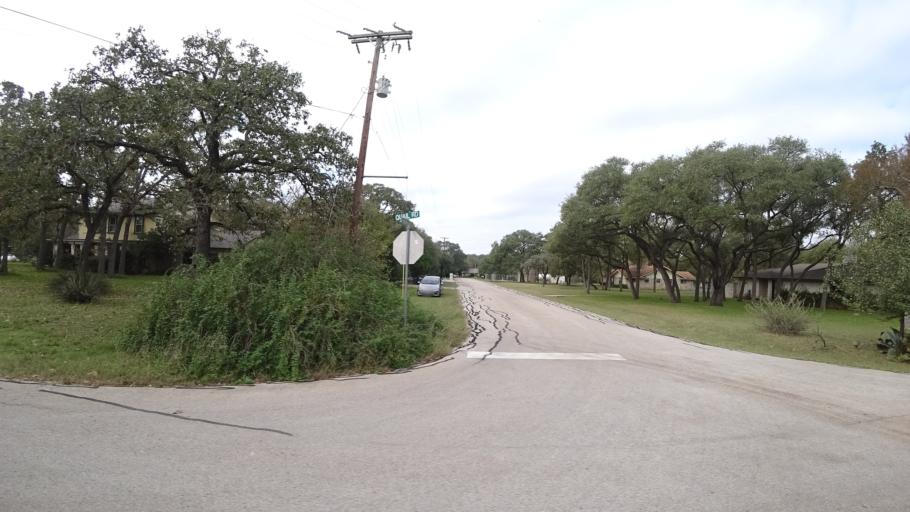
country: US
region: Texas
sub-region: Travis County
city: Shady Hollow
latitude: 30.1376
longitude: -97.8915
